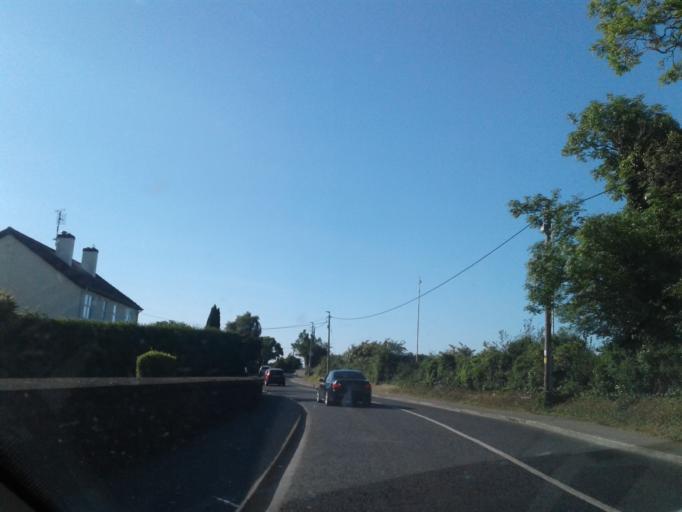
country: IE
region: Leinster
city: Foxrock
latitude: 53.2360
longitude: -6.1940
